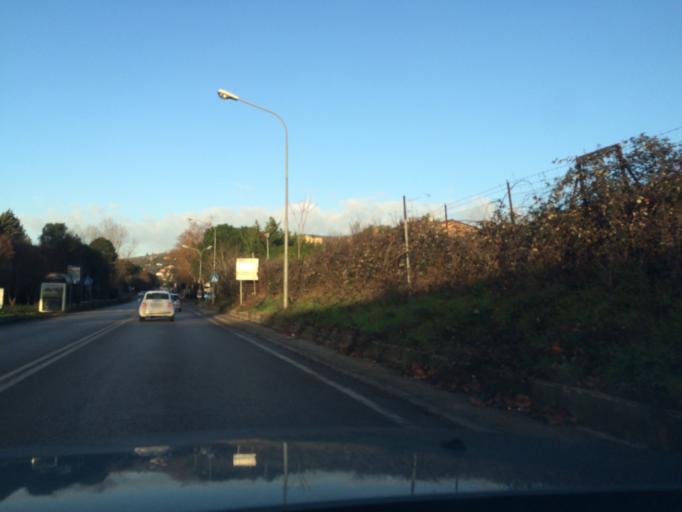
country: IT
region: Umbria
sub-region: Provincia di Perugia
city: Lacugnano
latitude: 43.1046
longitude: 12.3403
